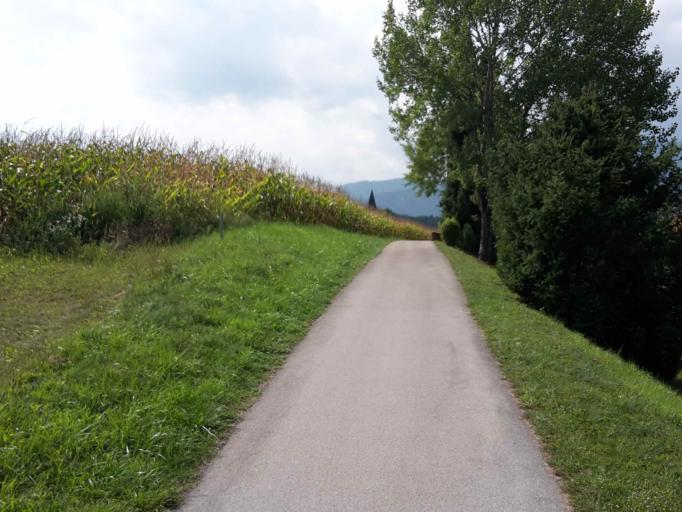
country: AT
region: Carinthia
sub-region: Politischer Bezirk Volkermarkt
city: Sittersdorf
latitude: 46.5815
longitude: 14.5652
